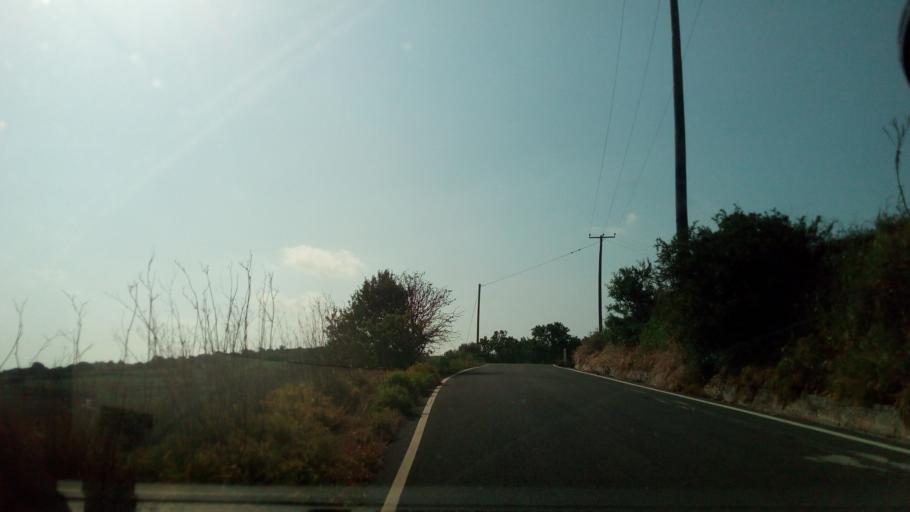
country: CY
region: Pafos
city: Polis
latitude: 34.9685
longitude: 32.3760
